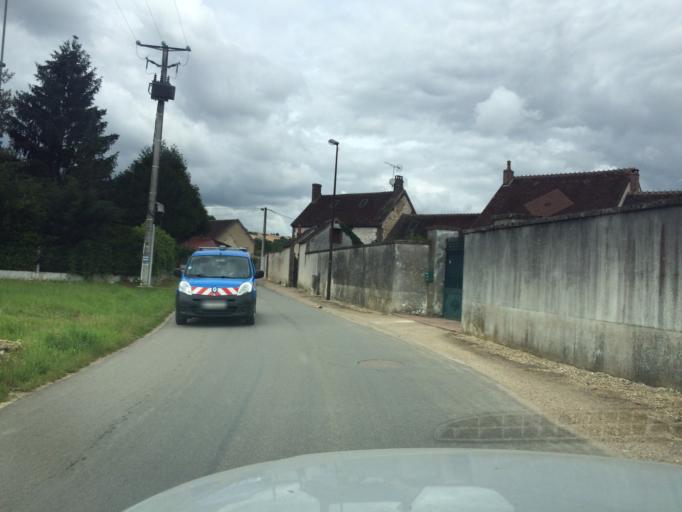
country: FR
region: Bourgogne
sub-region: Departement de l'Yonne
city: Aillant-sur-Tholon
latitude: 47.9264
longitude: 3.3560
